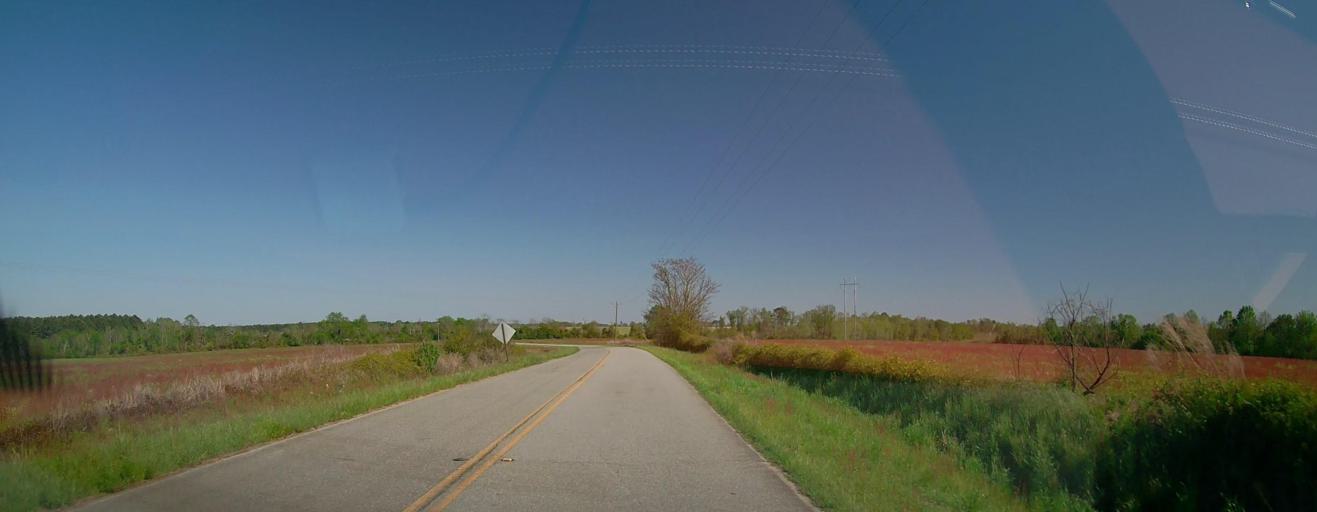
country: US
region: Georgia
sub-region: Pulaski County
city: Hawkinsville
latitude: 32.2478
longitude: -83.5820
